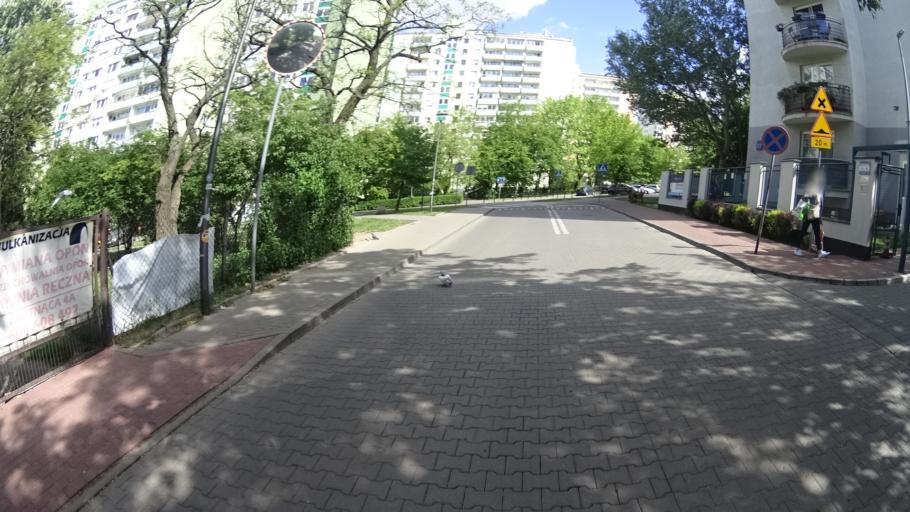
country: PL
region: Masovian Voivodeship
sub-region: Warszawa
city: Bemowo
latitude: 52.2760
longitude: 20.9147
